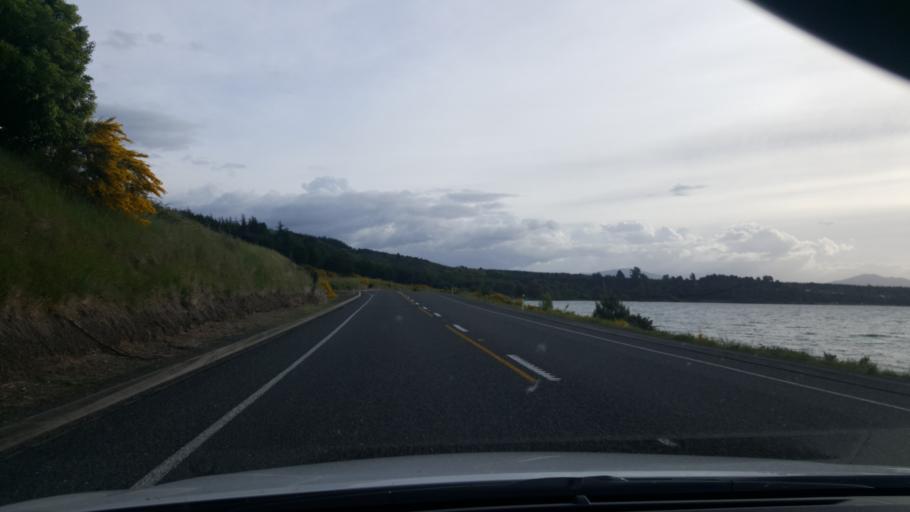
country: NZ
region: Waikato
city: Turangi
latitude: -38.8992
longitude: 175.9450
